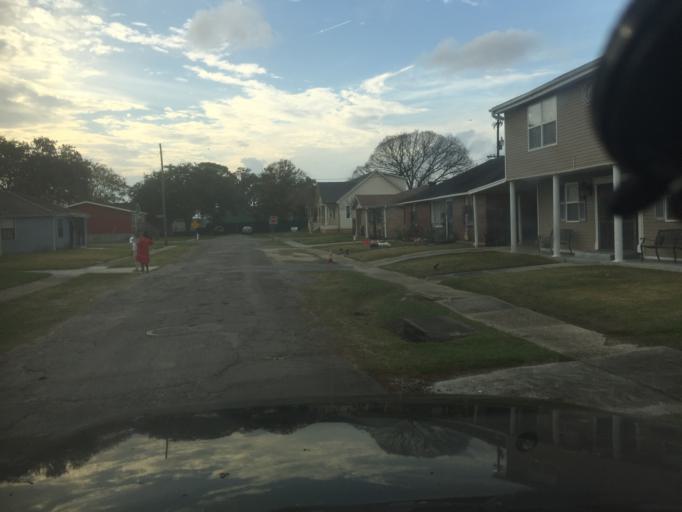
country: US
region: Louisiana
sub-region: Orleans Parish
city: New Orleans
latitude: 29.9870
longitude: -90.0822
